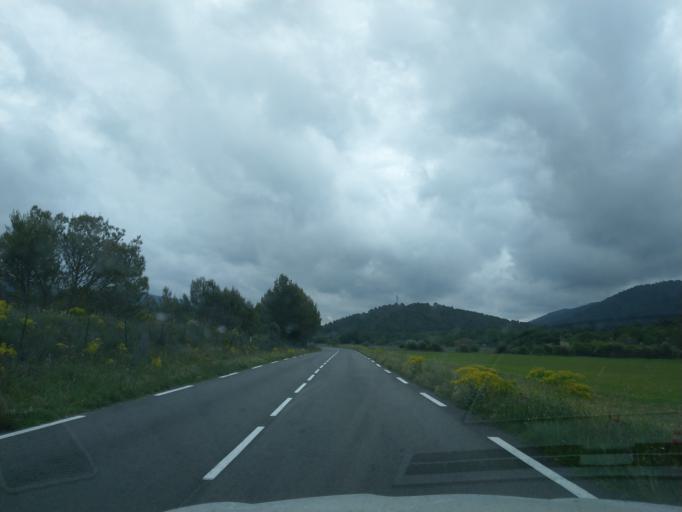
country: FR
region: Provence-Alpes-Cote d'Azur
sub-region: Departement du Var
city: Signes
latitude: 43.2837
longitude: 5.8321
